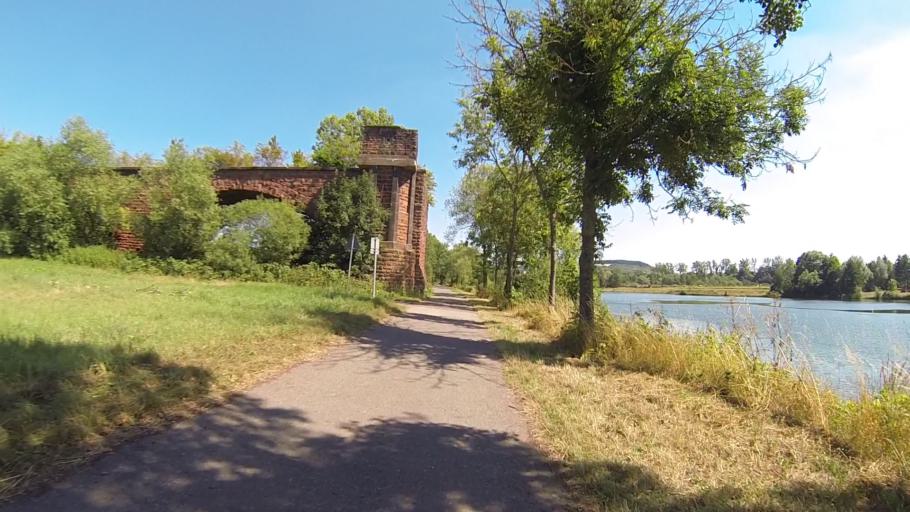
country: DE
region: Rheinland-Pfalz
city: Wasserliesch
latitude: 49.7025
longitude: 6.5589
